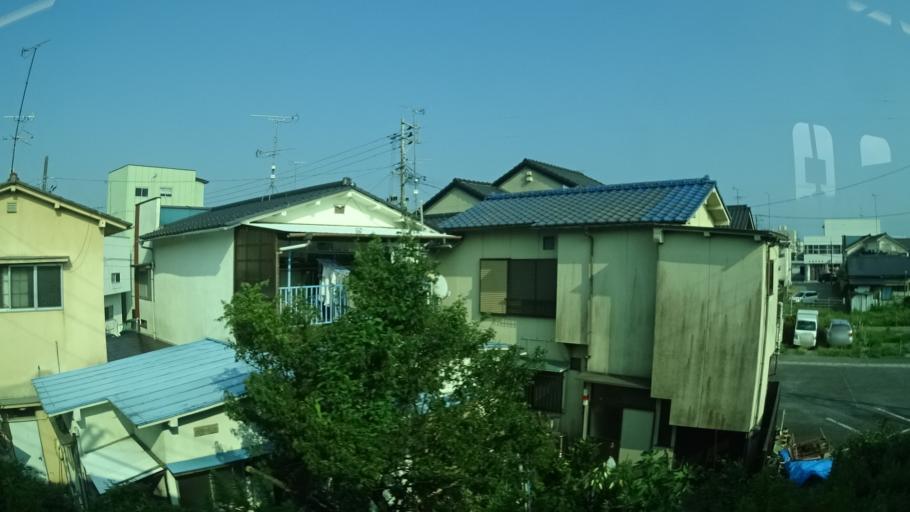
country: JP
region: Ibaraki
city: Kitaibaraki
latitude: 36.9175
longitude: 140.7957
